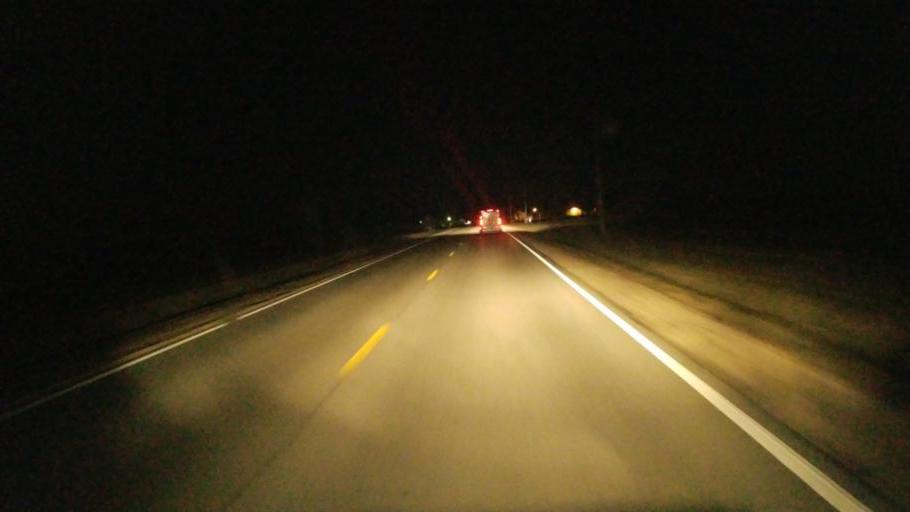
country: US
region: Illinois
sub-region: Henderson County
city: Oquawka
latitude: 40.8131
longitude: -90.9041
